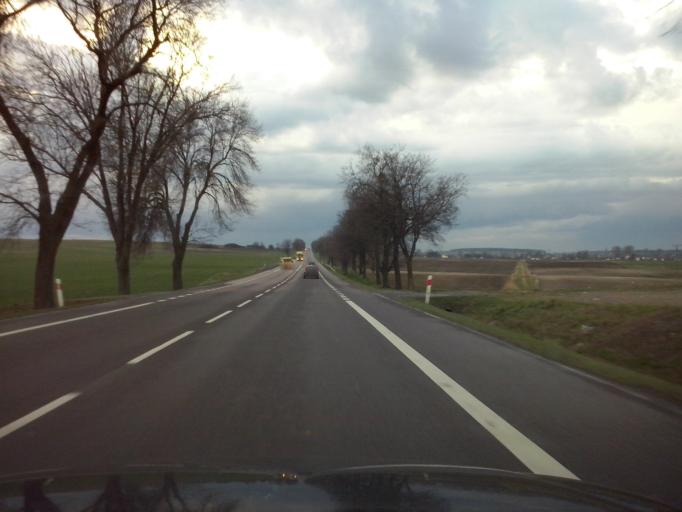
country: PL
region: Lublin Voivodeship
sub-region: Chelm
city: Chelm
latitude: 51.1660
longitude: 23.3748
